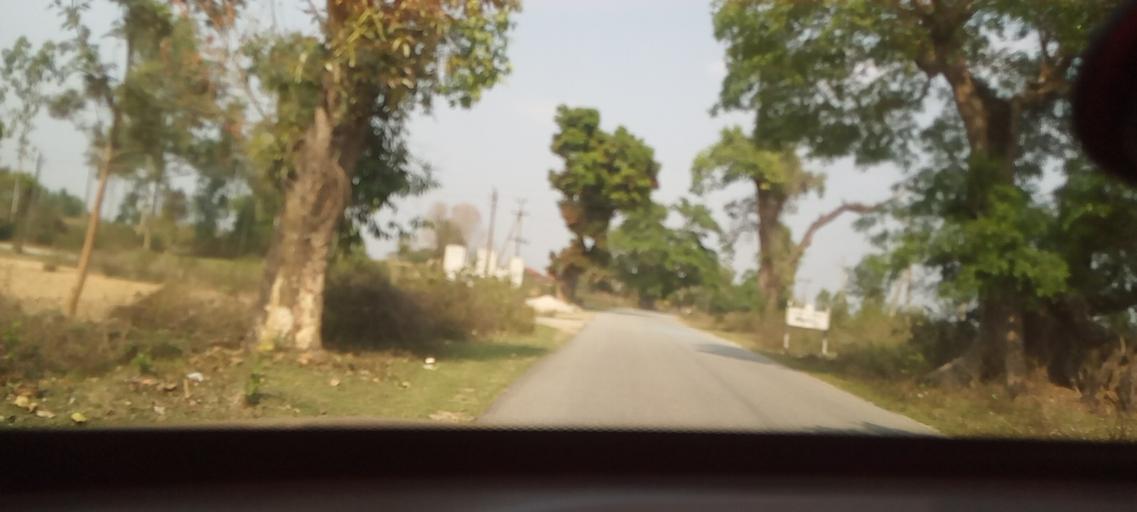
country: IN
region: Karnataka
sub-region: Hassan
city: Belur
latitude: 13.1790
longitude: 75.8254
